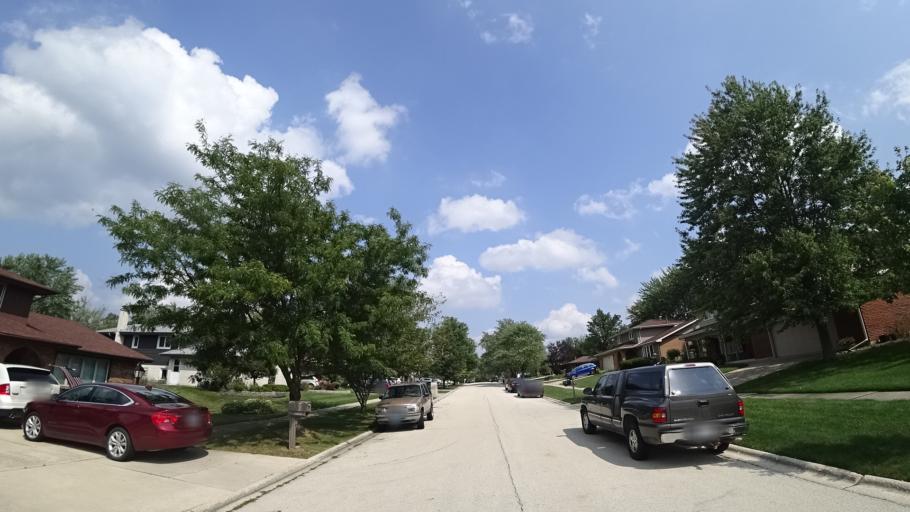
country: US
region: Illinois
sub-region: Will County
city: Goodings Grove
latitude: 41.6435
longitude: -87.9107
